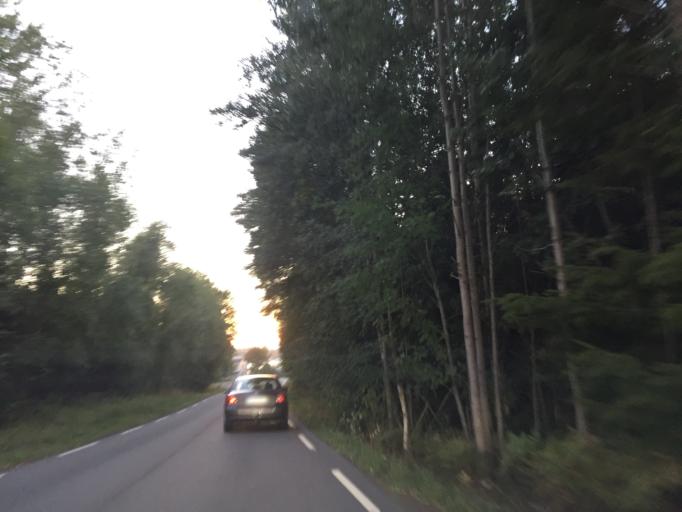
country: NO
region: Ostfold
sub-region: Moss
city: Moss
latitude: 59.4876
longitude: 10.6958
